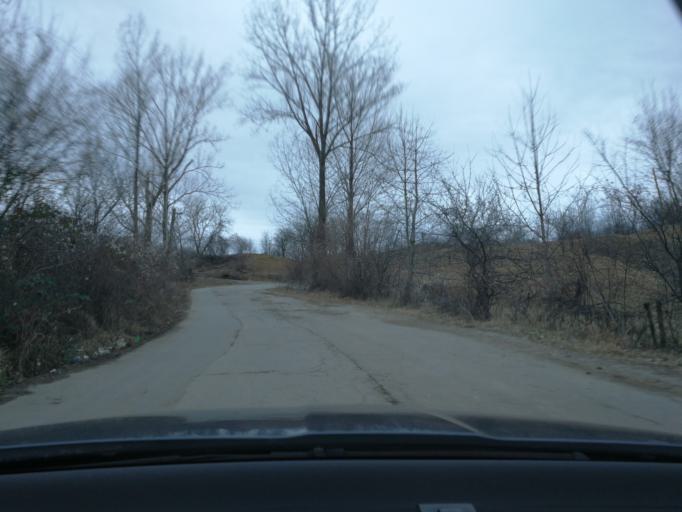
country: RO
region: Prahova
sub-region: Oras Breaza
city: Valea Tarsei
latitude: 45.1839
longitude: 25.6228
